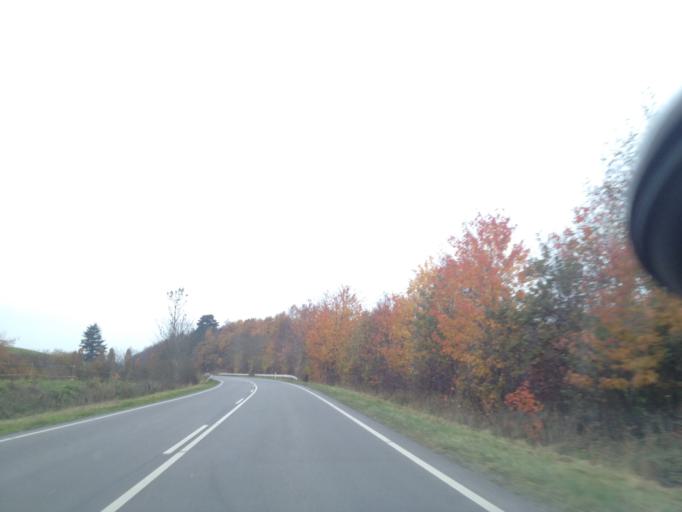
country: DK
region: South Denmark
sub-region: Nordfyns Kommune
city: Sonderso
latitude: 55.4364
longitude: 10.2287
